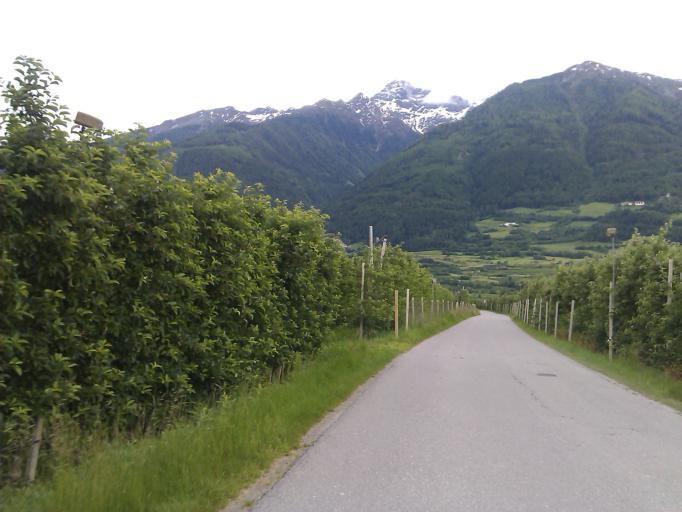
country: IT
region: Trentino-Alto Adige
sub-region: Bolzano
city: Prato Allo Stelvio
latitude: 46.6267
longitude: 10.6212
